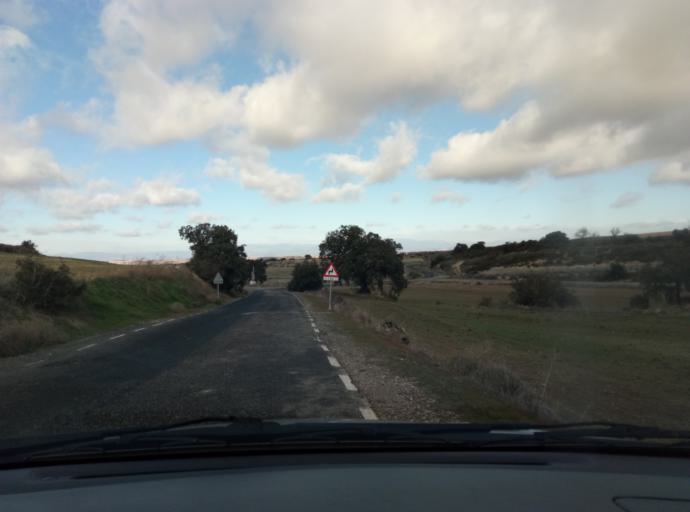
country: ES
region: Catalonia
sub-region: Provincia de Lleida
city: Nalec
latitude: 41.5897
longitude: 1.0848
